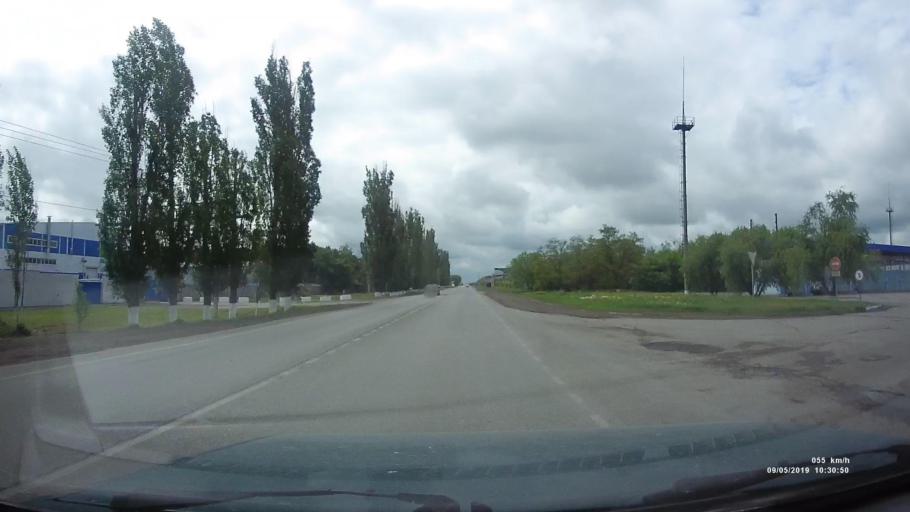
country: RU
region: Rostov
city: Azov
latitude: 47.0871
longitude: 39.4287
